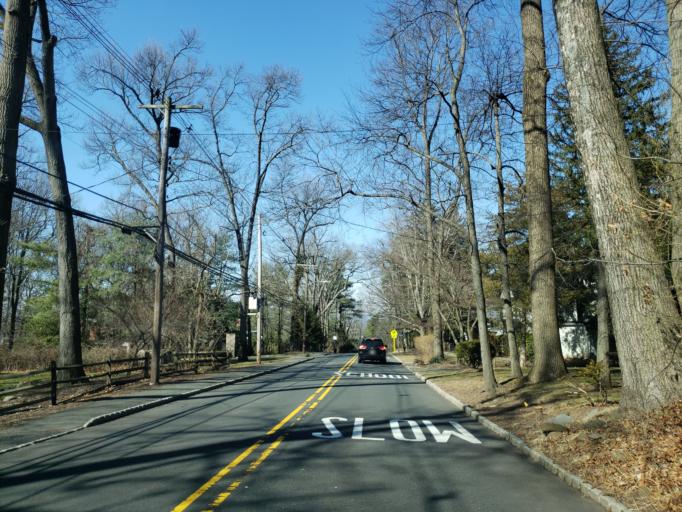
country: US
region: New Jersey
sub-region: Essex County
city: Short Hills
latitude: 40.7489
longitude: -74.3171
